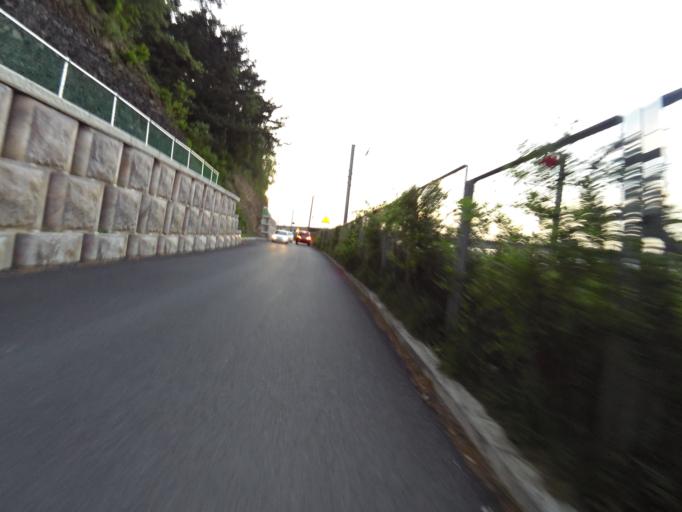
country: KR
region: Gyeongsangbuk-do
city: Gyeongsan-si
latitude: 35.8506
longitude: 128.7072
